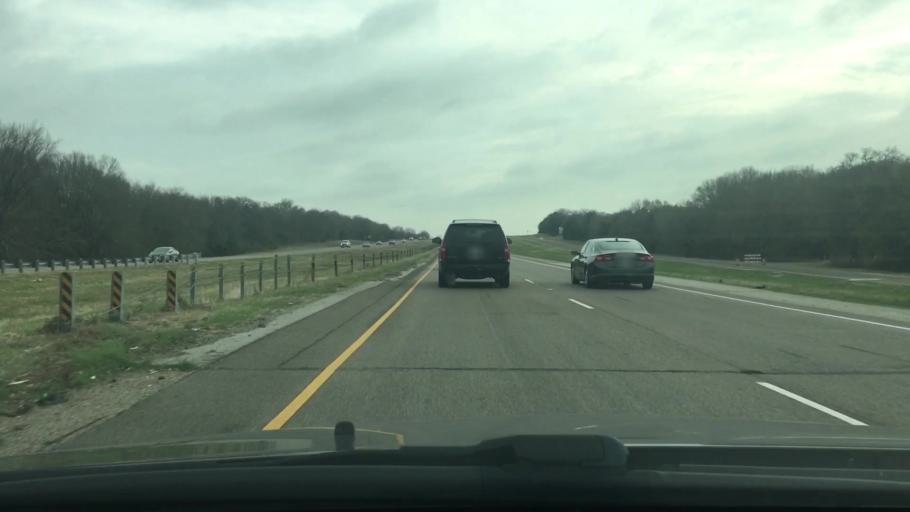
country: US
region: Texas
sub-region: Freestone County
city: Fairfield
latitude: 31.6465
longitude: -96.1595
